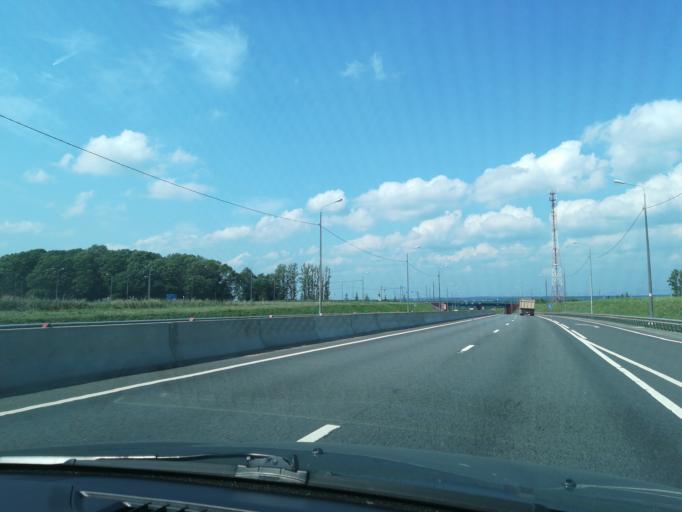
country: RU
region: Leningrad
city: Kingisepp
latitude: 59.5924
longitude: 28.7479
